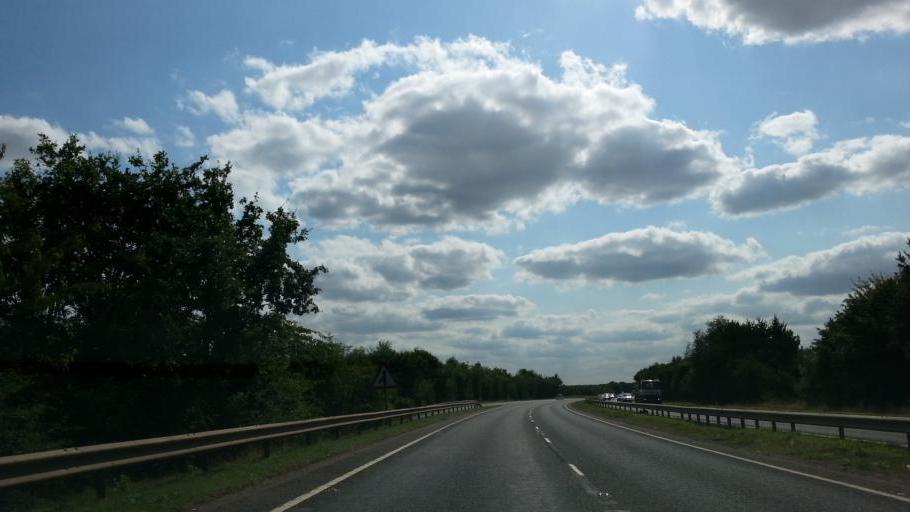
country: GB
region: England
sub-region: Leicestershire
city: Mountsorrel
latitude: 52.7089
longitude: -1.1238
